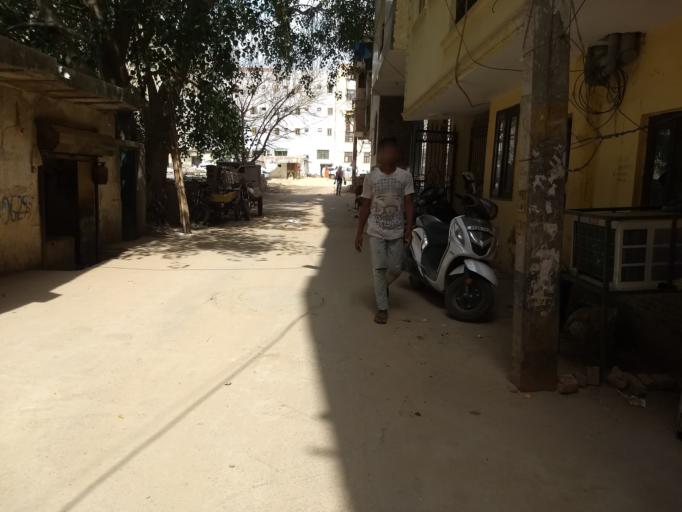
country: IN
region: NCT
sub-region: Central Delhi
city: Karol Bagh
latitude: 28.5406
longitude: 77.1256
